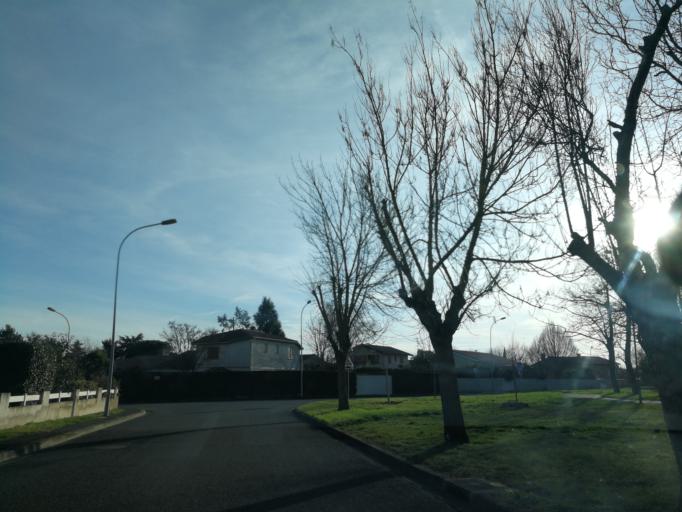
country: FR
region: Midi-Pyrenees
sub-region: Departement de la Haute-Garonne
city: L'Union
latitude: 43.6463
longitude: 1.4785
